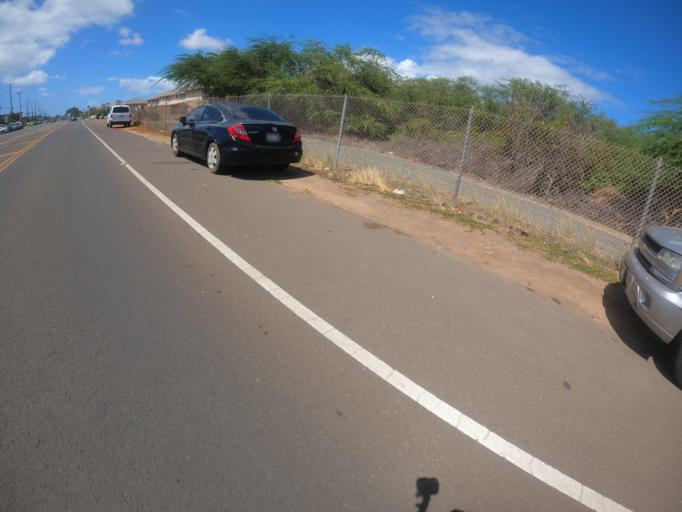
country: US
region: Hawaii
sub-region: Honolulu County
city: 'Ewa Beach
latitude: 21.3130
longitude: -158.0029
